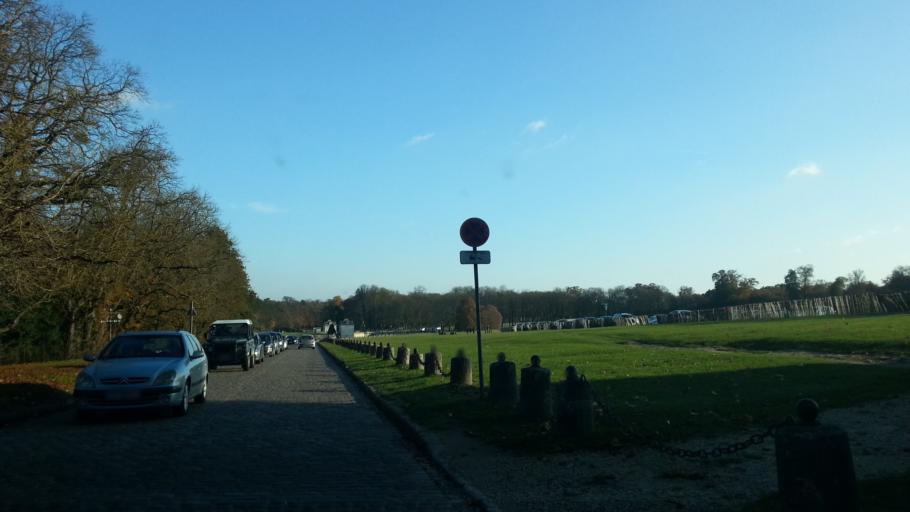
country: FR
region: Picardie
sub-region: Departement de l'Oise
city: Chantilly
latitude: 49.1940
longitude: 2.4806
